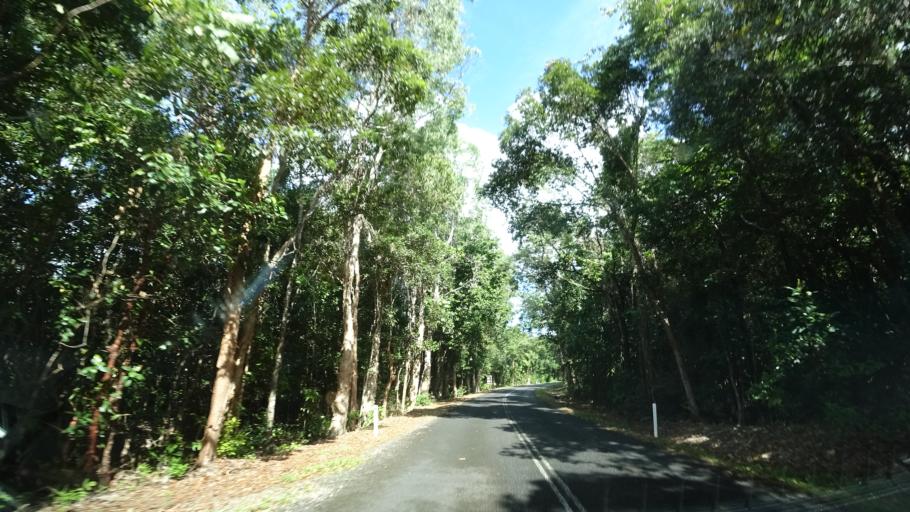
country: AU
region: Queensland
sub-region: Cairns
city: Port Douglas
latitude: -16.1747
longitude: 145.4400
